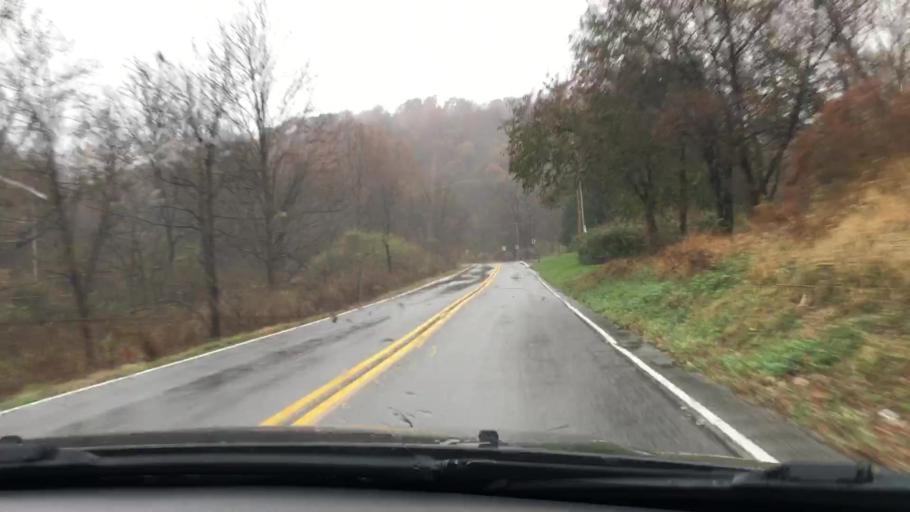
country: US
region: Pennsylvania
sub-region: York County
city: Shrewsbury
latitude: 39.7679
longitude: -76.7093
